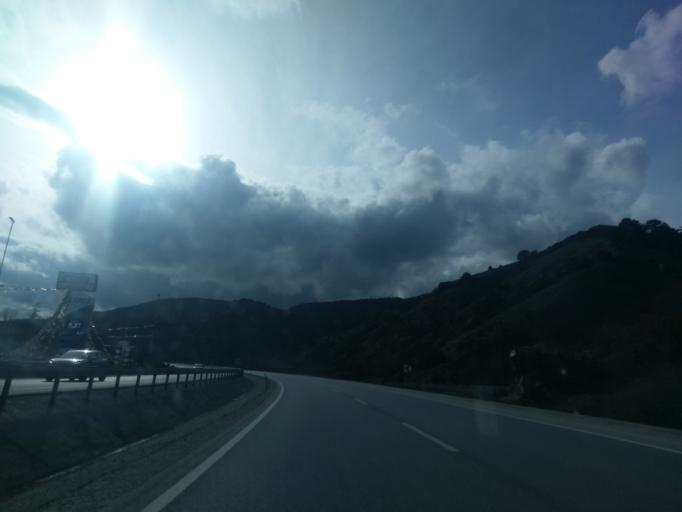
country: TR
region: Kuetahya
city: Sabuncu
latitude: 39.5559
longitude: 30.0641
